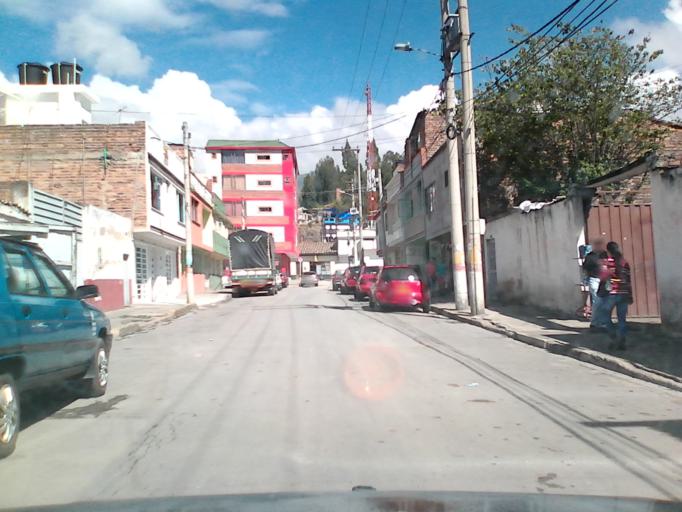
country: CO
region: Boyaca
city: Duitama
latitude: 5.8244
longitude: -73.0376
